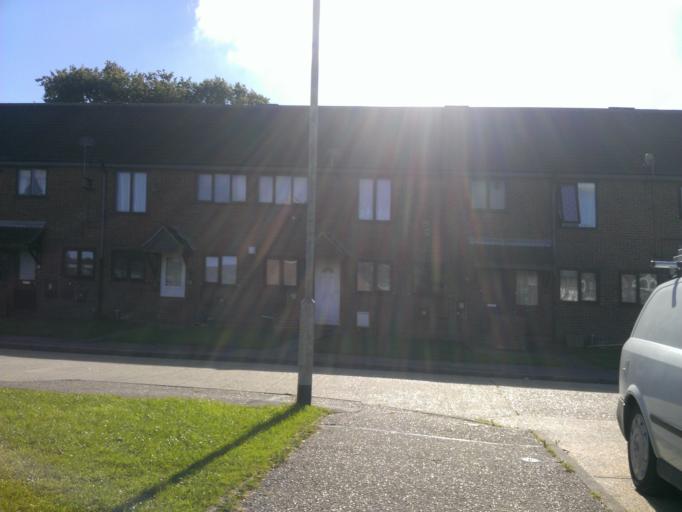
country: GB
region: England
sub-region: Essex
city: Clacton-on-Sea
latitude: 51.8038
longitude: 1.1496
